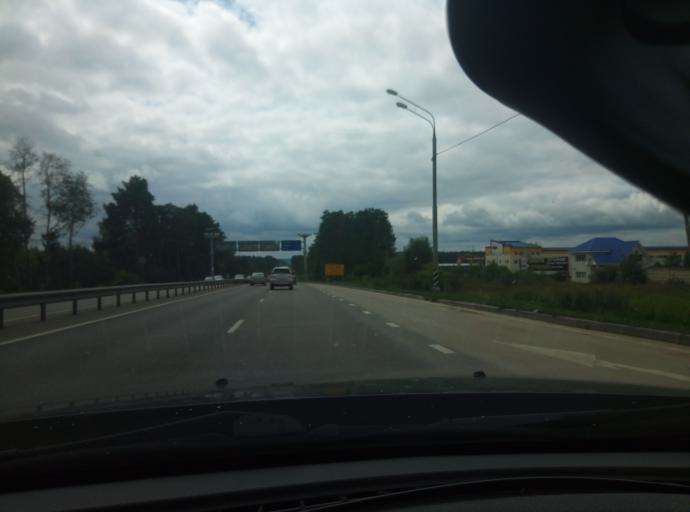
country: RU
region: Kaluga
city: Obninsk
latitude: 55.0731
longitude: 36.6263
